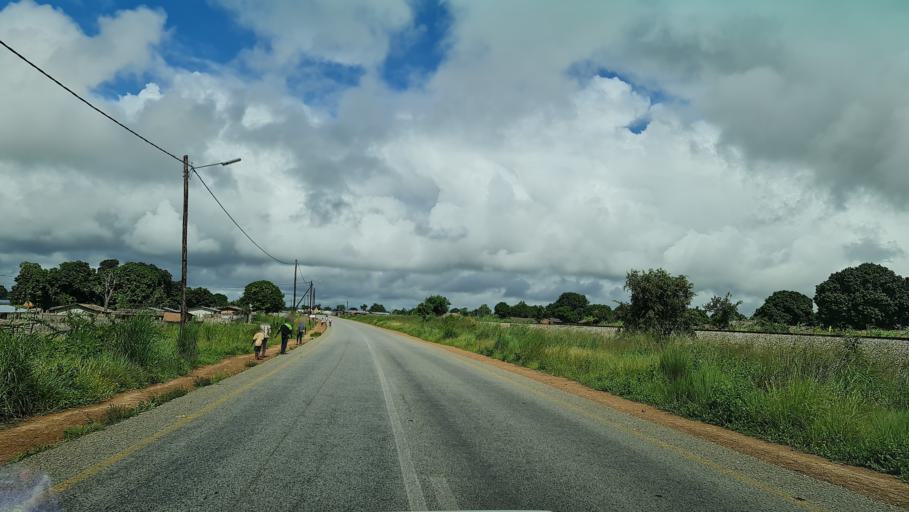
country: MZ
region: Nampula
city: Nampula
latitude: -15.0257
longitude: 38.4626
